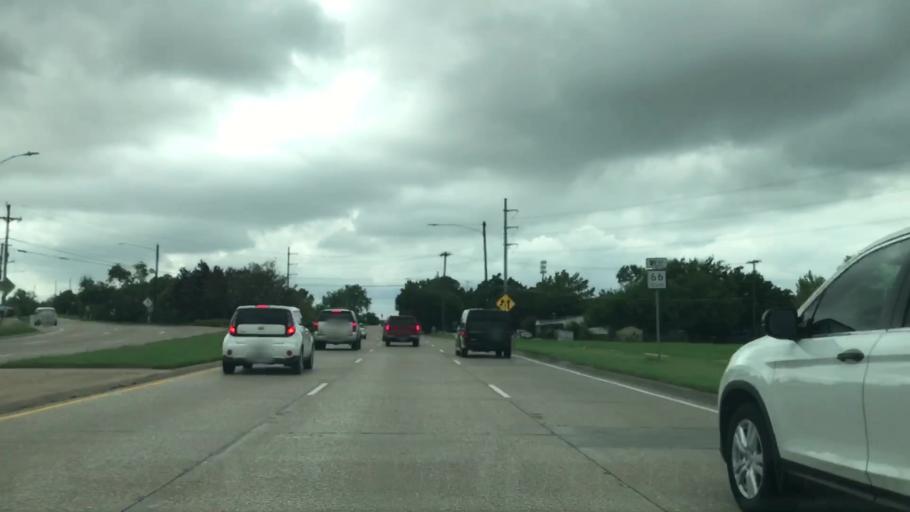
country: US
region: Texas
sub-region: Dallas County
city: Garland
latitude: 32.9087
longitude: -96.6226
